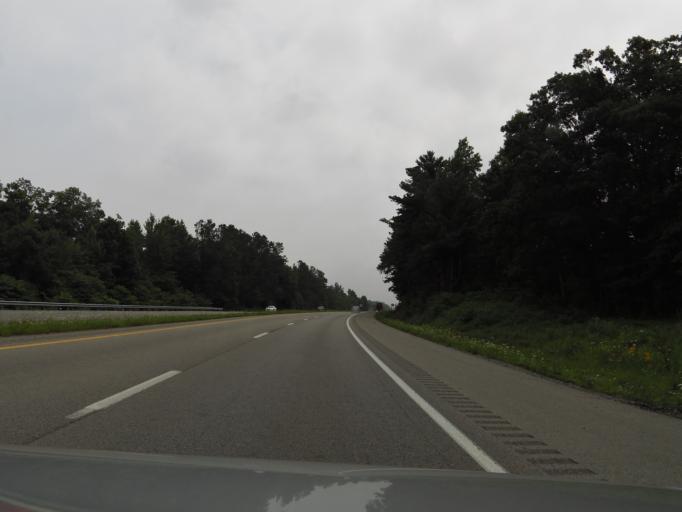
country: US
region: Kentucky
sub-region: Muhlenberg County
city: Central City
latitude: 37.2958
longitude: -87.0800
